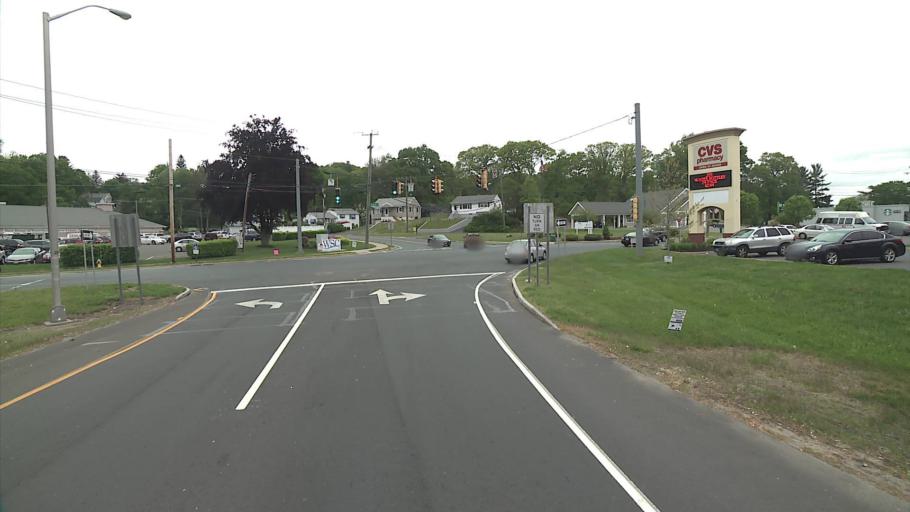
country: US
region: Connecticut
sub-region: New Haven County
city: Waterbury
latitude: 41.5514
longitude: -73.0646
